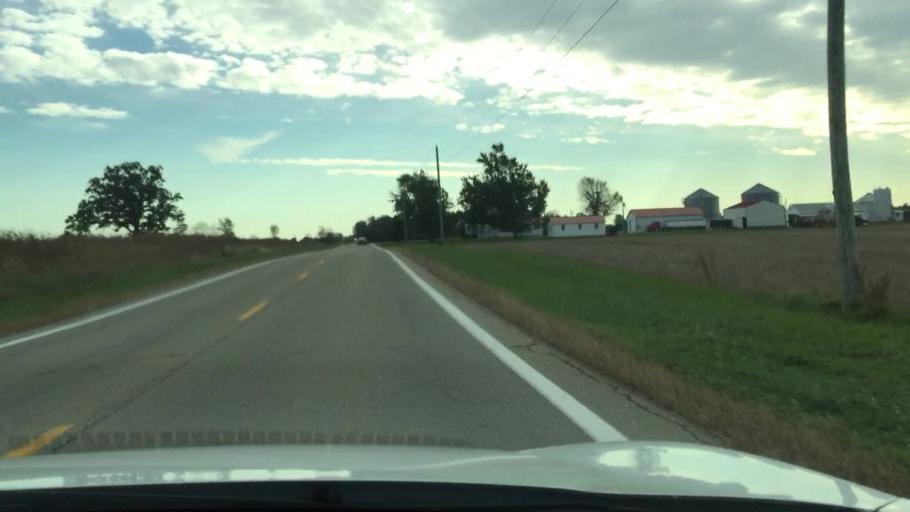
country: US
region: Ohio
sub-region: Champaign County
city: Mechanicsburg
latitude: 40.1118
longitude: -83.5370
